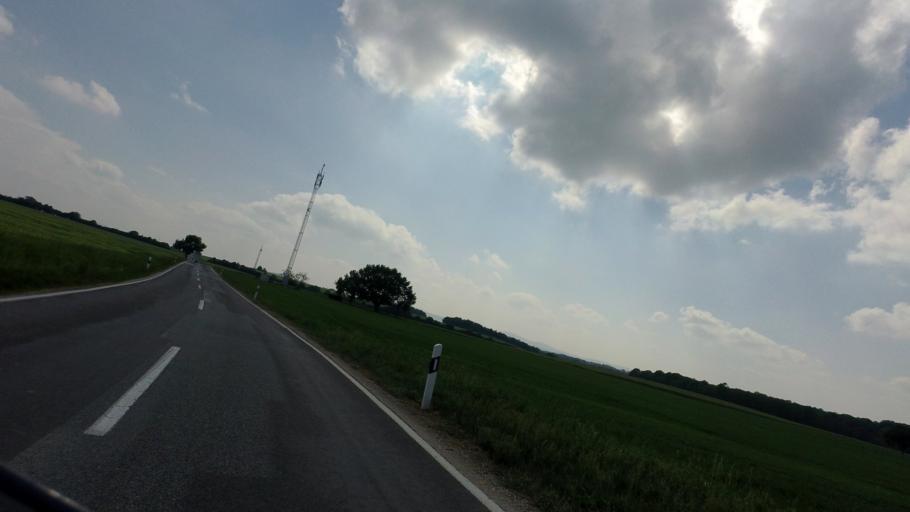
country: DE
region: Saxony
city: Weissenberg
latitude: 51.2157
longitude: 14.6644
